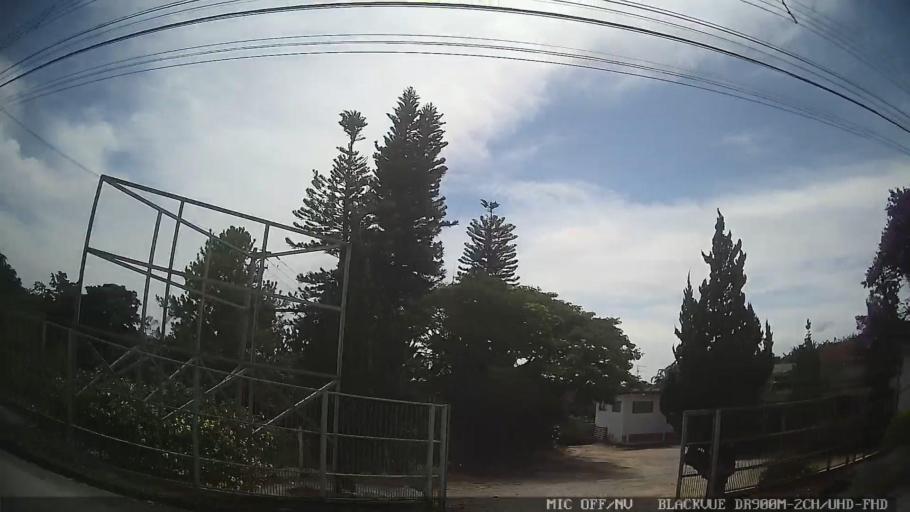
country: BR
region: Sao Paulo
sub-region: Santa Isabel
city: Santa Isabel
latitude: -23.3813
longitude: -46.1777
